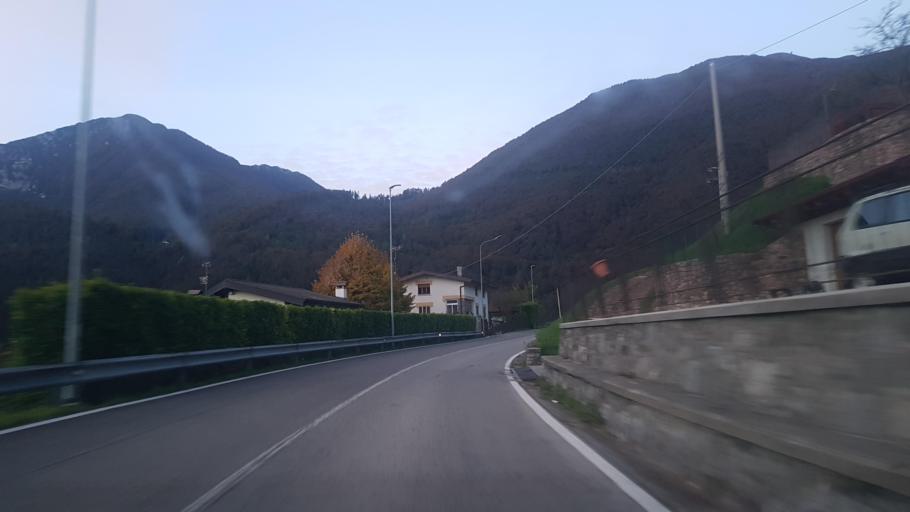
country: IT
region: Friuli Venezia Giulia
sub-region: Provincia di Udine
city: Chiaulis
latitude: 46.3823
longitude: 12.9729
